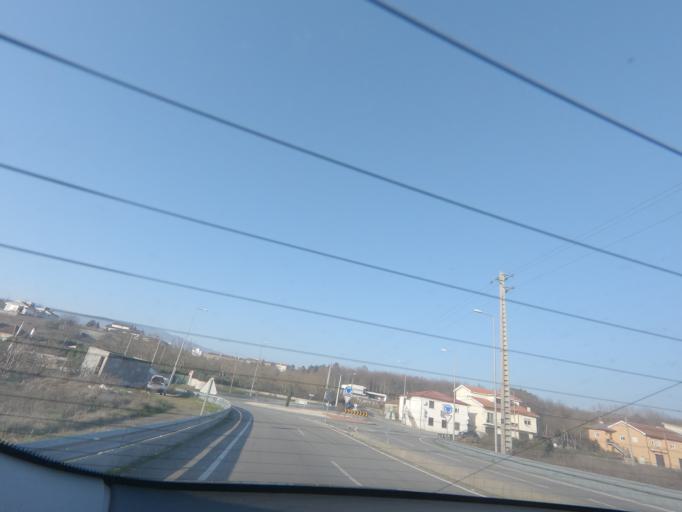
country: PT
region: Vila Real
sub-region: Vila Real
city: Vila Real
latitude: 41.2897
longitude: -7.7224
